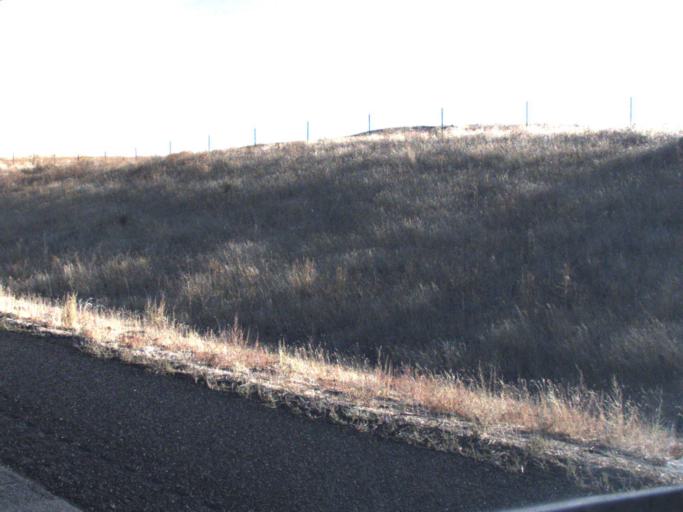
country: US
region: Washington
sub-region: Franklin County
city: Basin City
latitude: 46.5380
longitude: -119.0125
